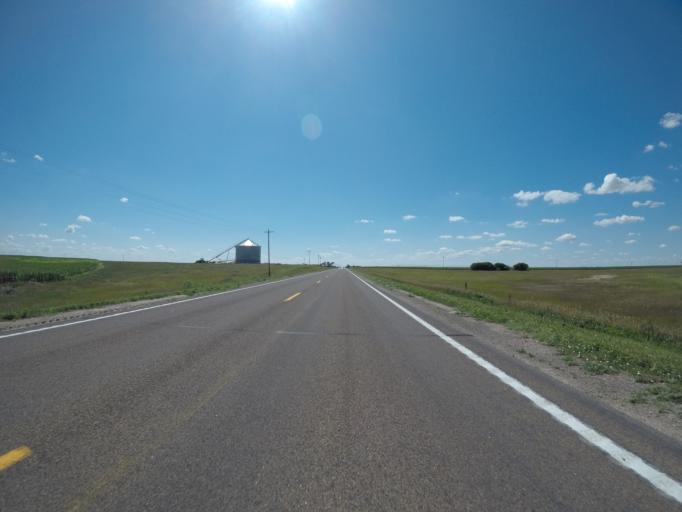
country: US
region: Nebraska
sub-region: Chase County
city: Imperial
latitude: 40.5375
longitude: -101.7771
